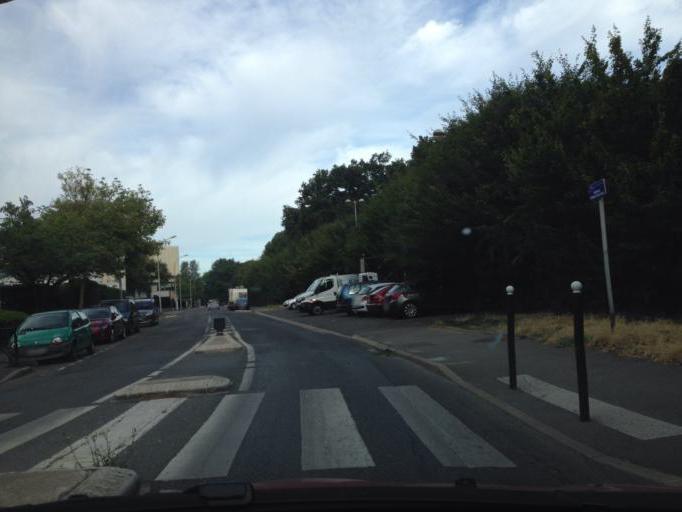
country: FR
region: Ile-de-France
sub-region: Departement des Hauts-de-Seine
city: Meudon
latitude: 48.7899
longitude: 2.2310
